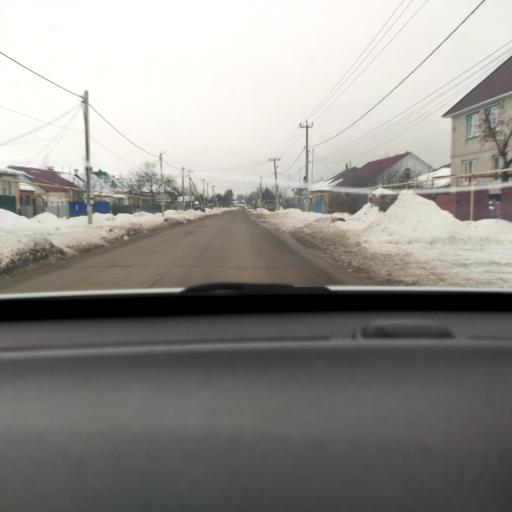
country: RU
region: Voronezj
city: Volya
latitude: 51.7468
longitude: 39.4881
